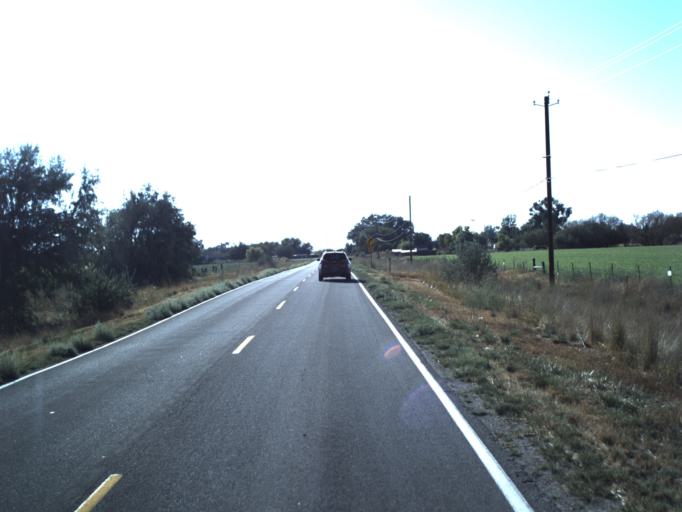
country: US
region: Utah
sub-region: Weber County
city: Hooper
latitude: 41.1399
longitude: -112.1182
